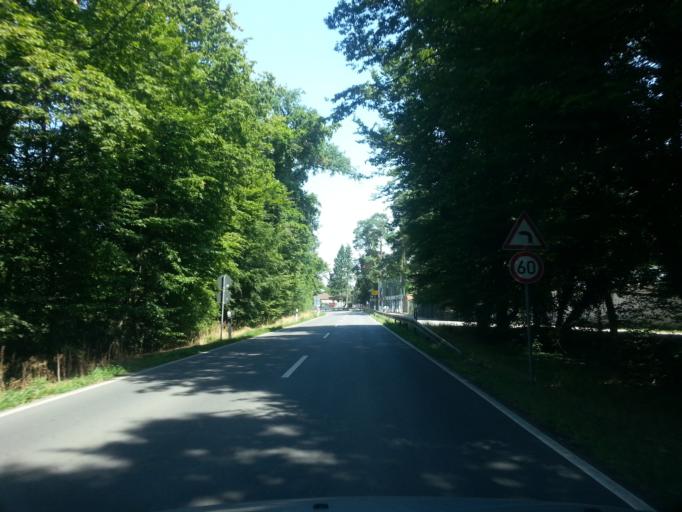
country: DE
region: Hesse
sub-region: Regierungsbezirk Darmstadt
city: Einhausen
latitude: 49.6624
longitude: 8.5425
